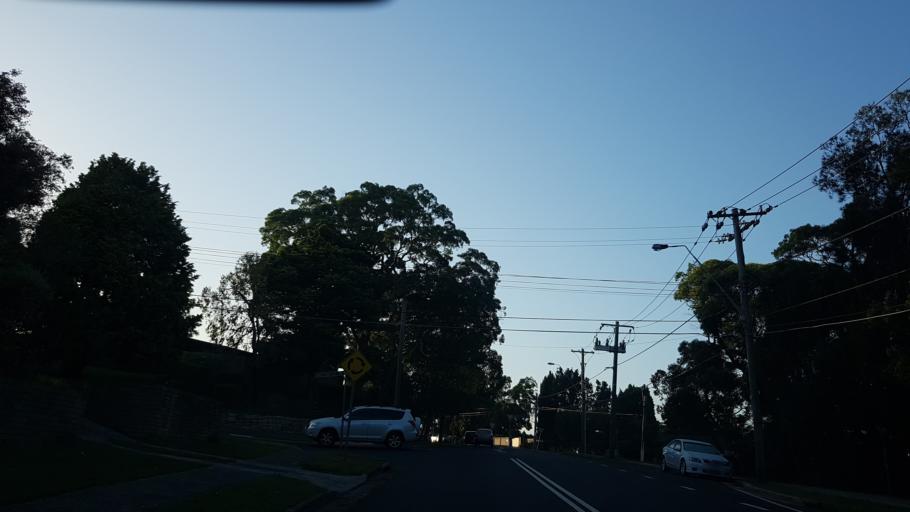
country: AU
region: New South Wales
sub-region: Warringah
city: Narraweena
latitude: -33.7316
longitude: 151.2771
